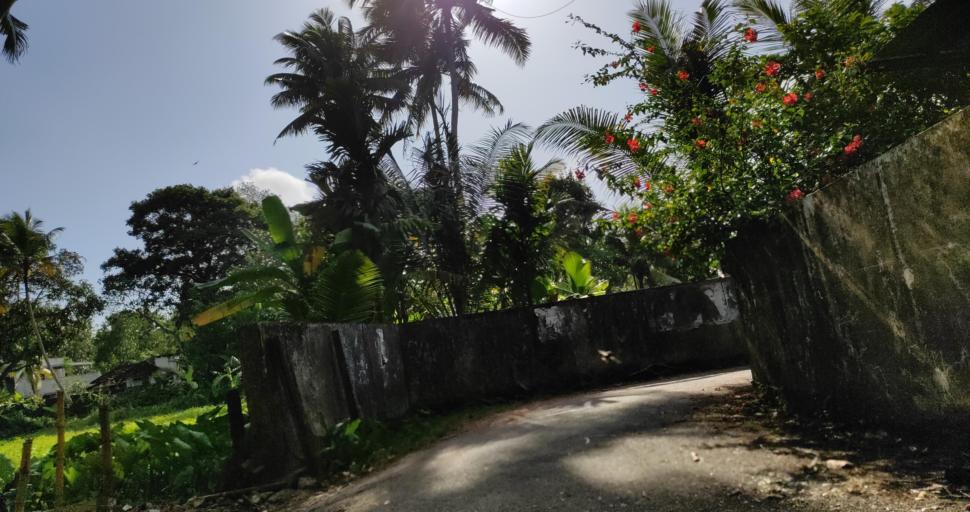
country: IN
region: Kerala
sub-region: Alappuzha
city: Shertallai
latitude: 9.6035
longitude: 76.3303
